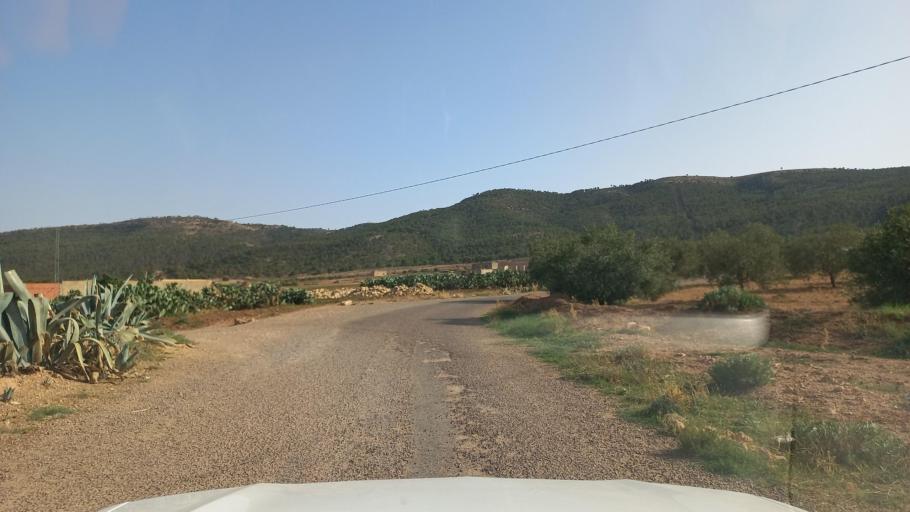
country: TN
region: Al Qasrayn
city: Kasserine
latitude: 35.3425
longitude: 8.8349
